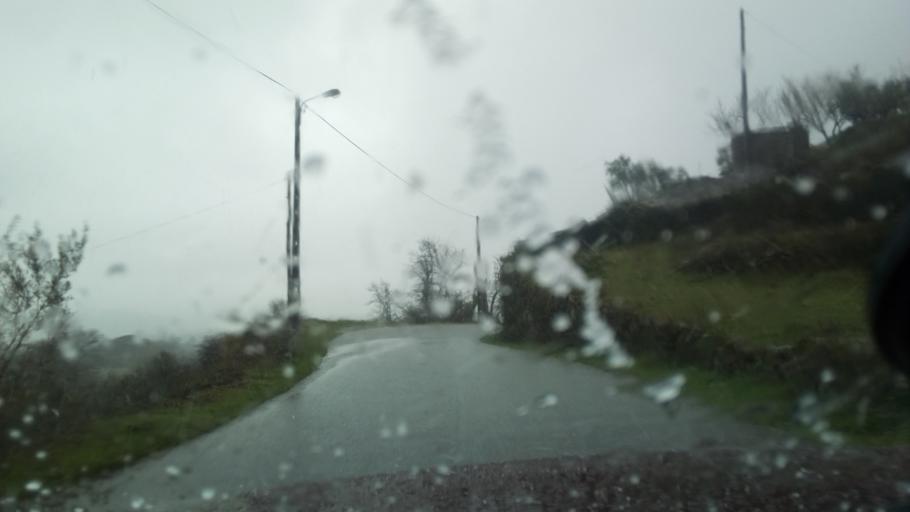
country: PT
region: Guarda
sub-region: Fornos de Algodres
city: Fornos de Algodres
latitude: 40.5411
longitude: -7.4640
